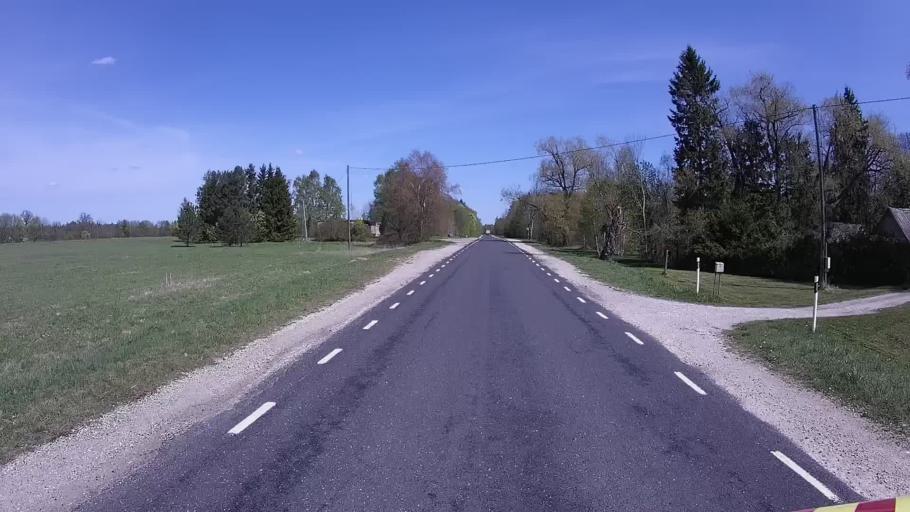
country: EE
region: Laeaene
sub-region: Ridala Parish
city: Uuemoisa
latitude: 59.0154
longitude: 23.7907
